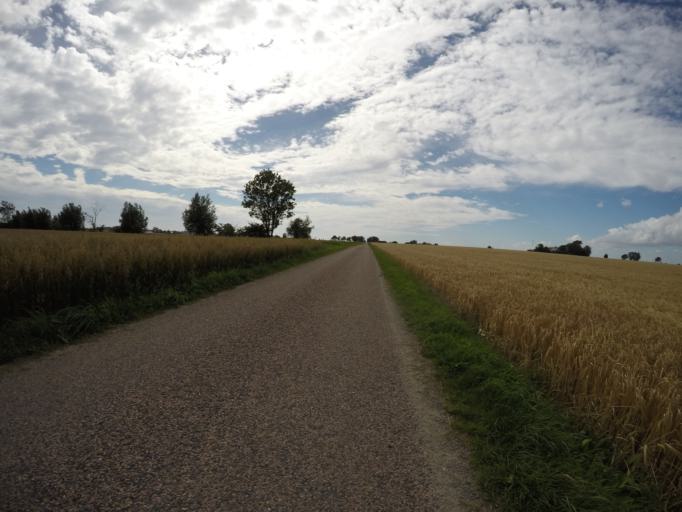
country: SE
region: Skane
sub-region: Simrishamns Kommun
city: Simrishamn
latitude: 55.4191
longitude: 14.1774
